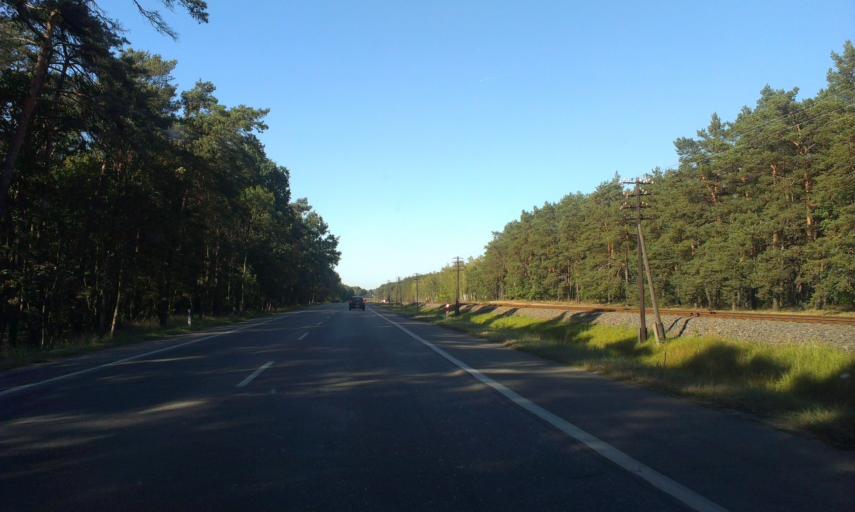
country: PL
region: Kujawsko-Pomorskie
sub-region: Powiat torunski
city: Lysomice
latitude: 53.0592
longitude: 18.6177
